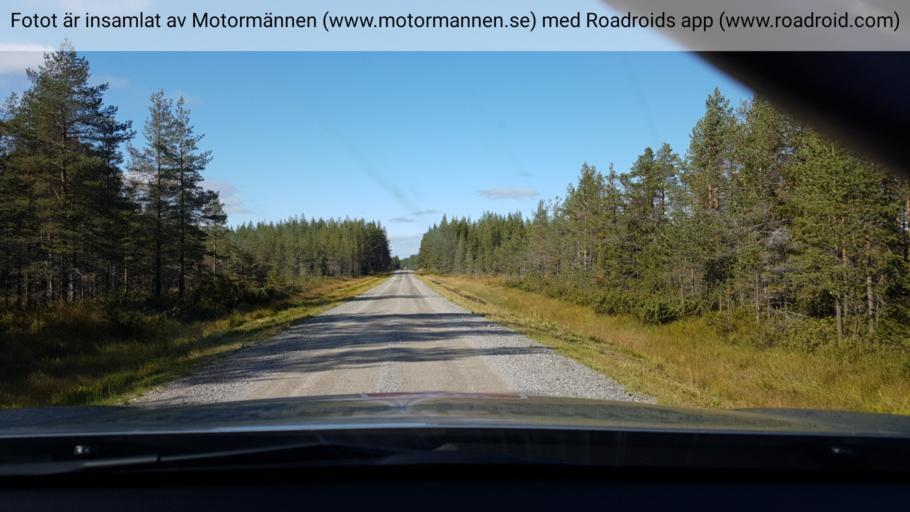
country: SE
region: Norrbotten
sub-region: Arvidsjaurs Kommun
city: Arvidsjaur
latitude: 65.2073
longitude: 19.1499
